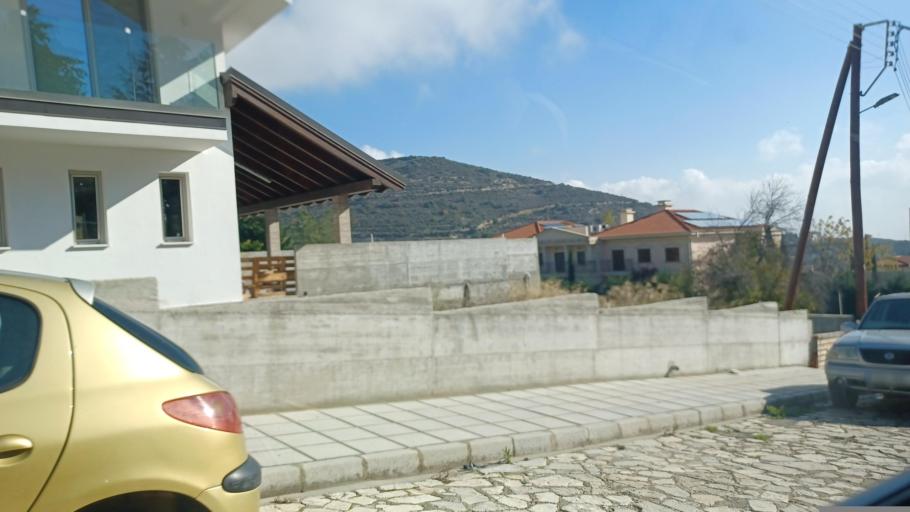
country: CY
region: Larnaka
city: Kofinou
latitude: 34.8526
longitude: 33.3028
